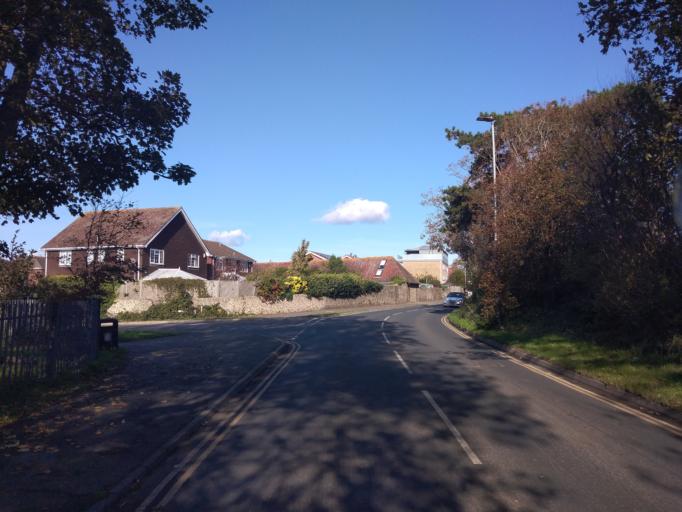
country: GB
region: England
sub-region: East Sussex
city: Seaford
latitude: 50.7764
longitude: 0.1172
